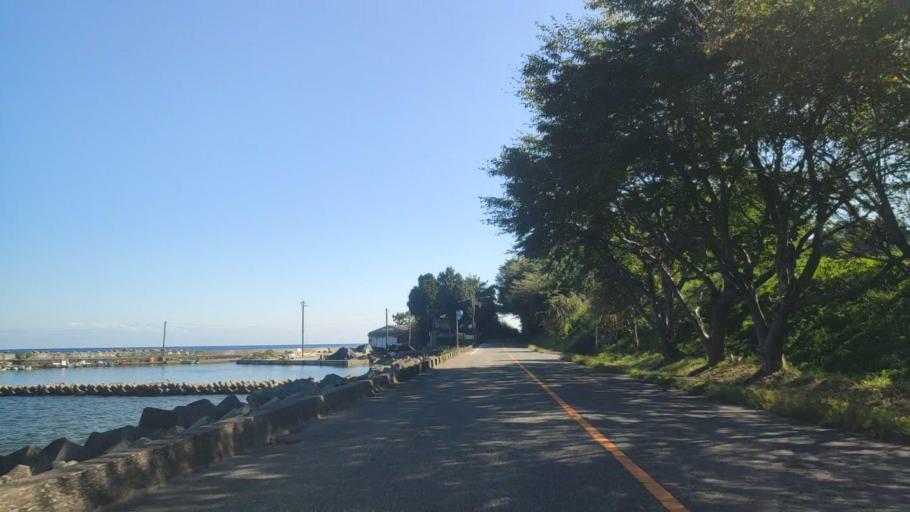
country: JP
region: Ishikawa
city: Nanao
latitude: 37.2750
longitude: 137.0968
